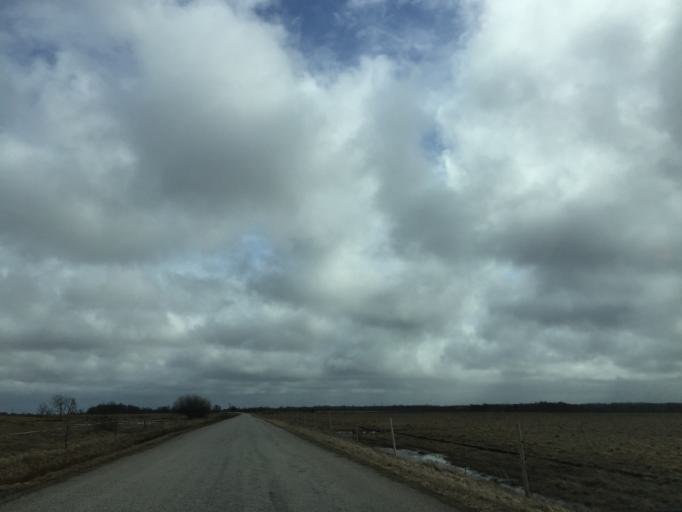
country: EE
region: Laeaene
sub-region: Lihula vald
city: Lihula
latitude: 58.7300
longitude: 23.8803
